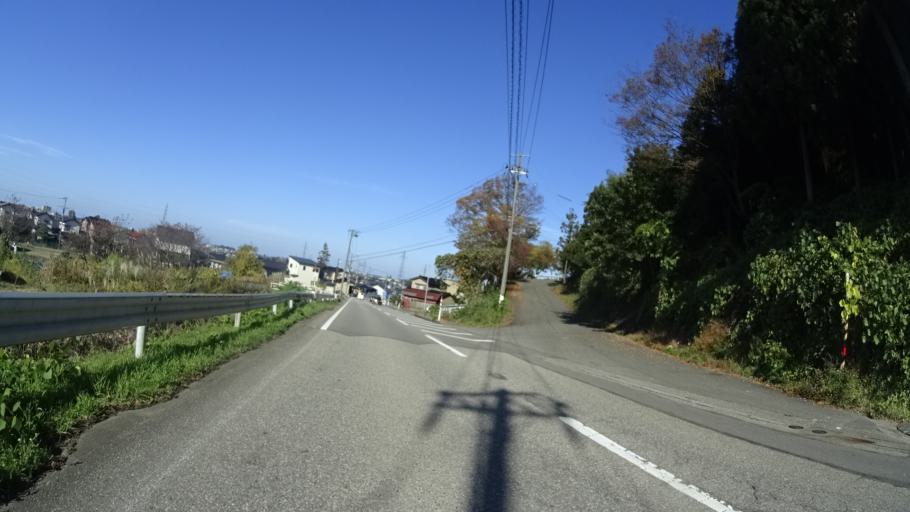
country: JP
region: Ishikawa
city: Tsurugi-asahimachi
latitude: 36.4813
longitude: 136.6159
